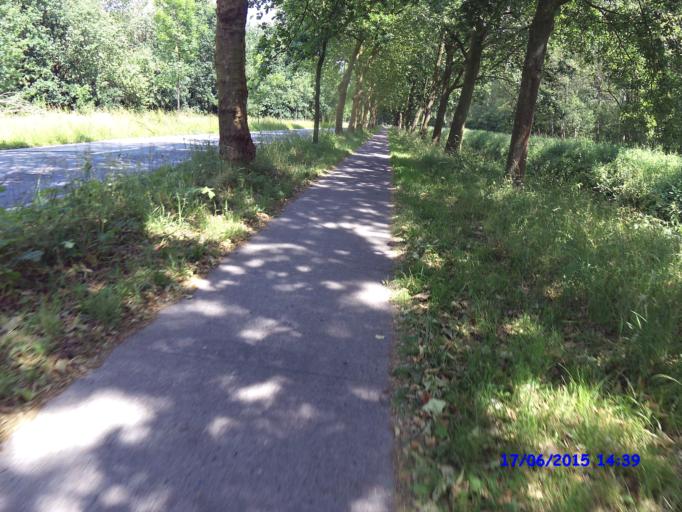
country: BE
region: Flanders
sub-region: Provincie Antwerpen
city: Schelle
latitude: 51.1365
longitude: 4.3586
